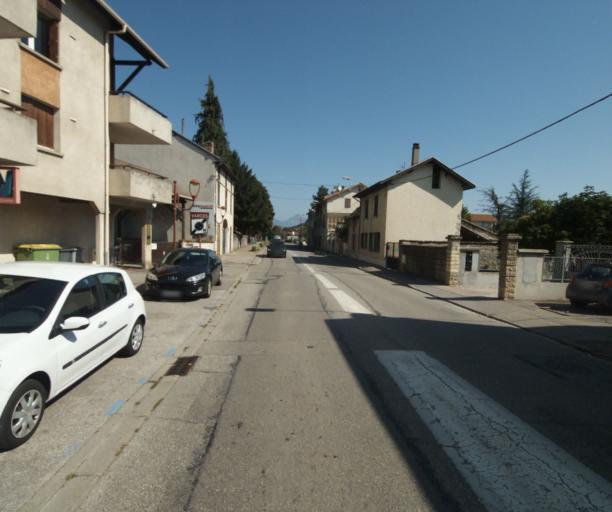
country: FR
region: Rhone-Alpes
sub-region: Departement de l'Isere
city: Allieres-et-Risset
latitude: 45.0873
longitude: 5.6833
